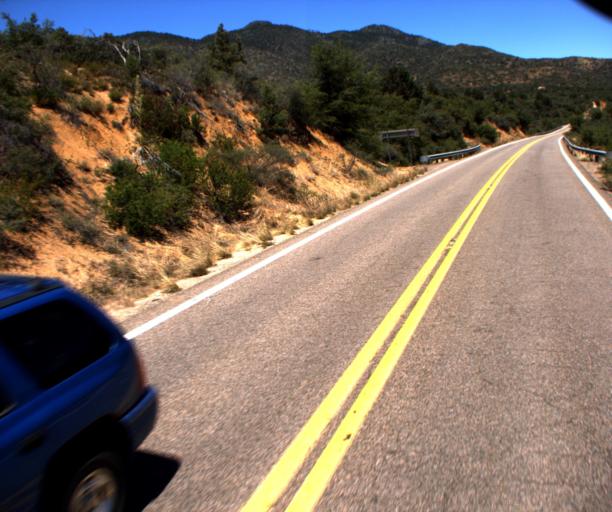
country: US
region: Arizona
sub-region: Gila County
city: Globe
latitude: 33.2465
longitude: -110.7825
